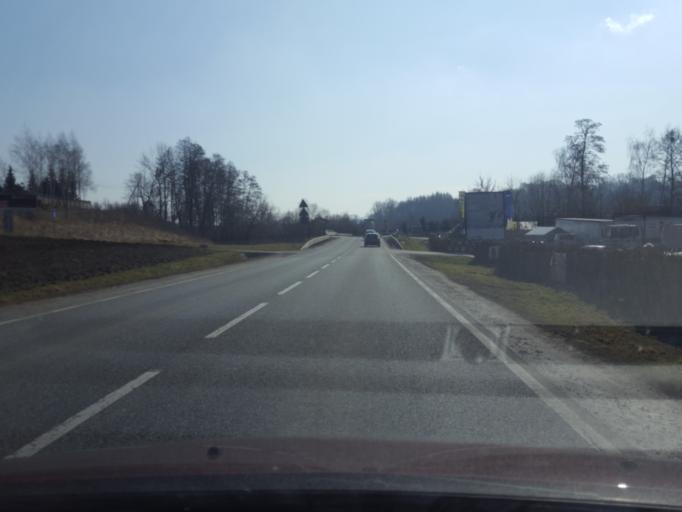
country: PL
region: Lesser Poland Voivodeship
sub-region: Powiat brzeski
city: Czchow
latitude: 49.8523
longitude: 20.6720
